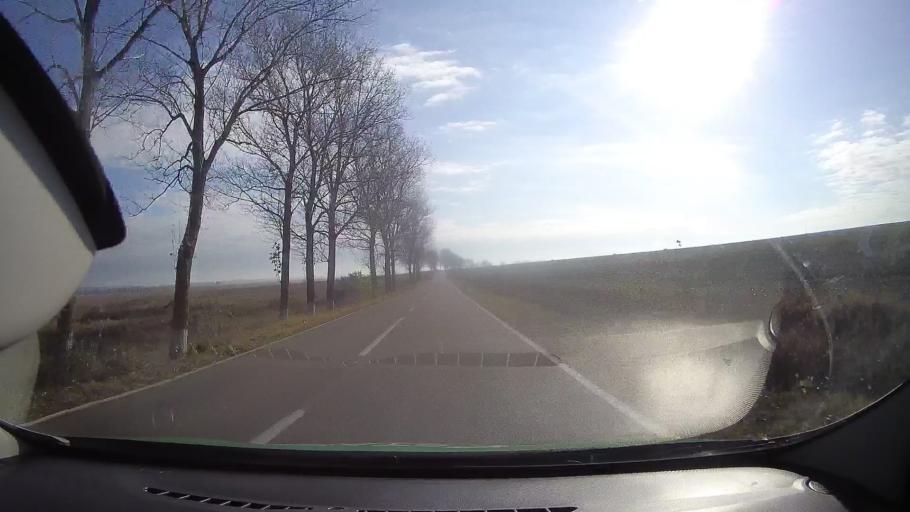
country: RO
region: Tulcea
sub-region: Comuna Mahmudia
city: Mahmudia
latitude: 45.0685
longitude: 29.1017
